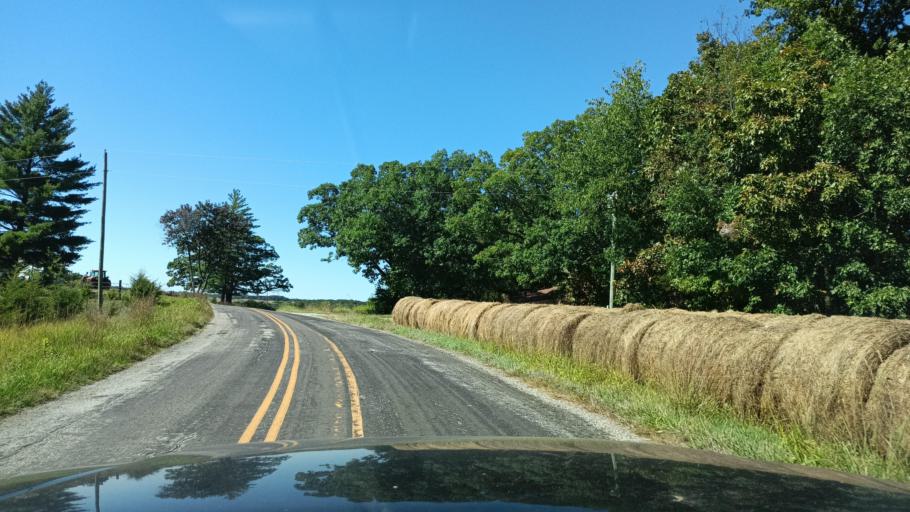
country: US
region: Missouri
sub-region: Scotland County
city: Memphis
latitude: 40.3523
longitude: -92.3416
